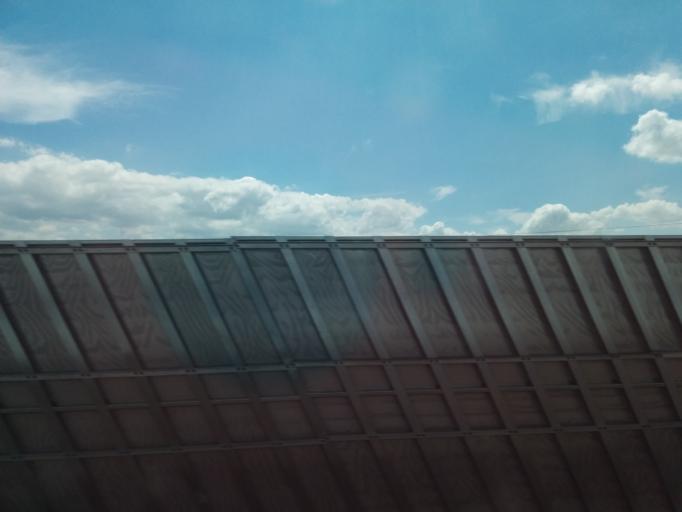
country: JP
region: Shiga Prefecture
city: Youkaichi
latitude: 35.1747
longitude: 136.2127
